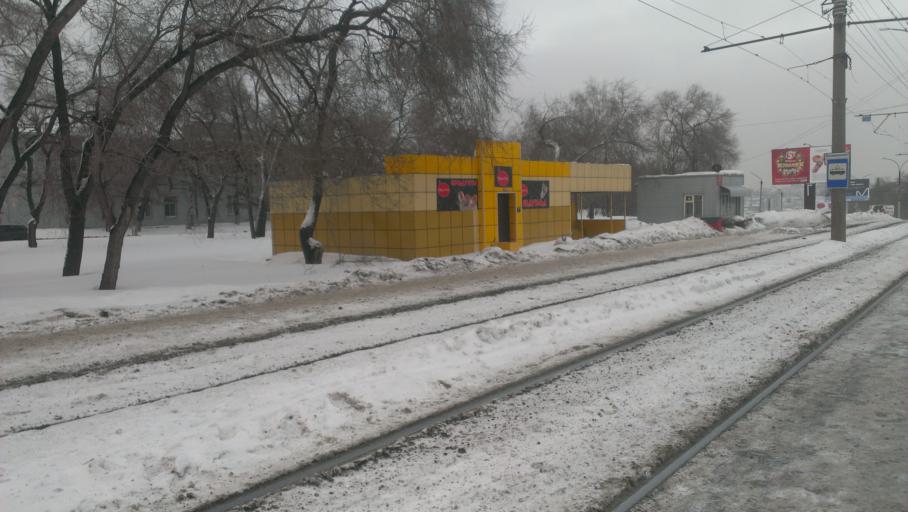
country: RU
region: Altai Krai
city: Zaton
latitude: 53.3191
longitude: 83.7873
